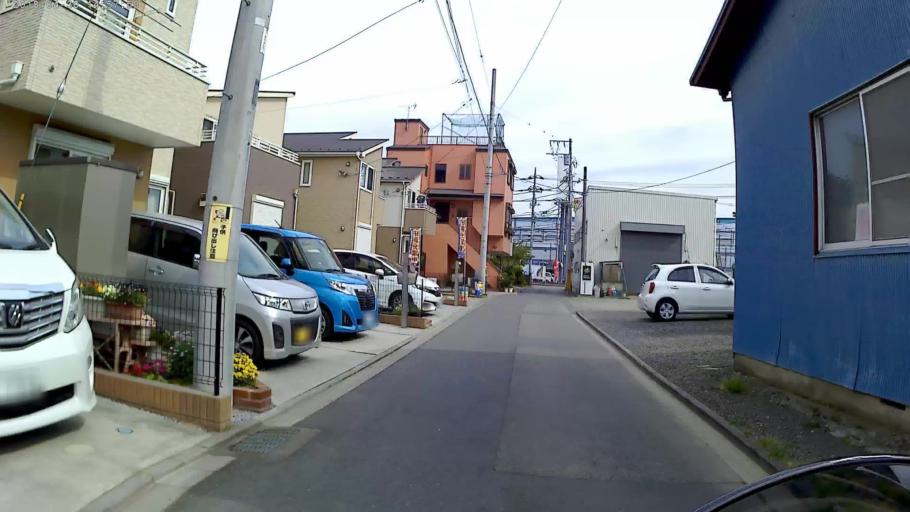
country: JP
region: Kanagawa
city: Zama
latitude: 35.5558
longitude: 139.3457
